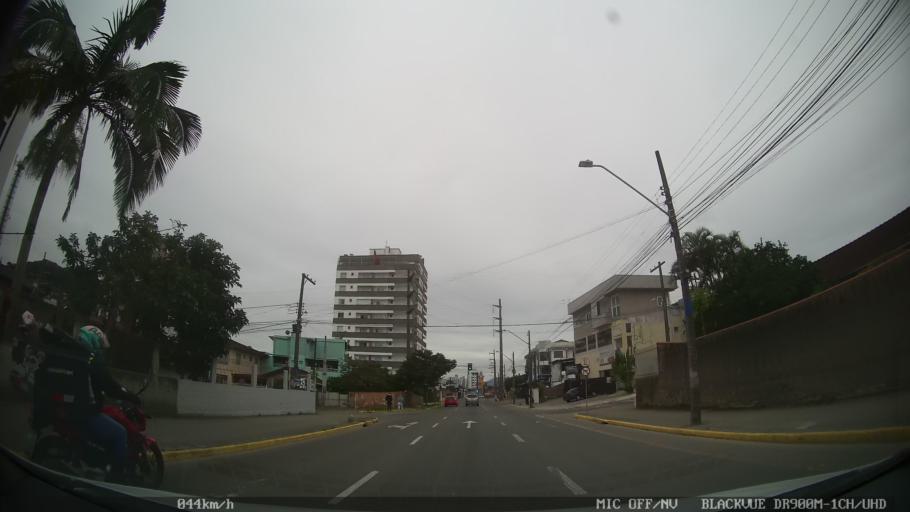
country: BR
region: Santa Catarina
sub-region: Joinville
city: Joinville
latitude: -26.2751
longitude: -48.8304
